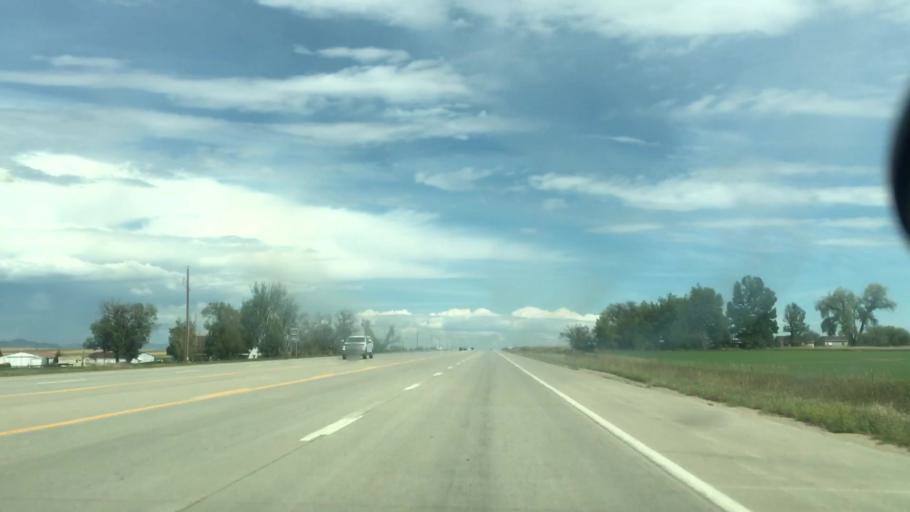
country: US
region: Colorado
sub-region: Boulder County
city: Longmont
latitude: 40.2125
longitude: -105.1023
